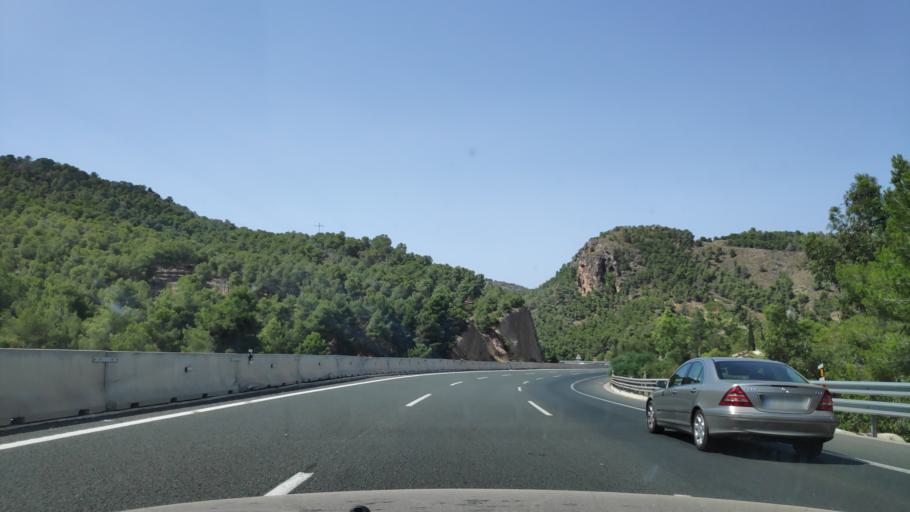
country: ES
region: Murcia
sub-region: Murcia
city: Murcia
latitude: 37.8964
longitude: -1.1422
